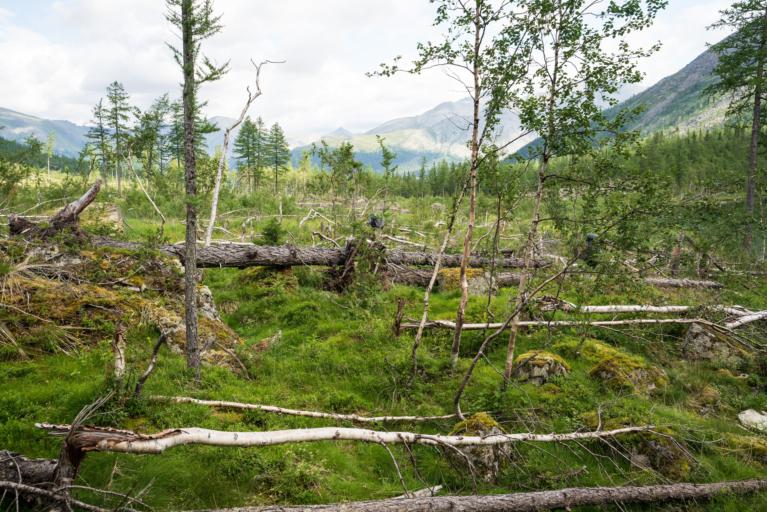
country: RU
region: Komi Republic
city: Synya
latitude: 64.8543
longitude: 59.3369
